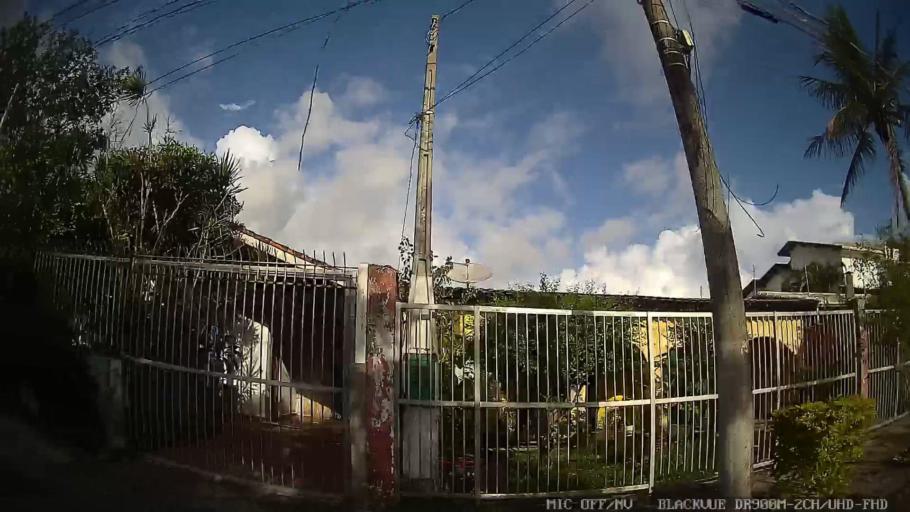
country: BR
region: Sao Paulo
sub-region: Itanhaem
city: Itanhaem
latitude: -24.1971
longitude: -46.8122
